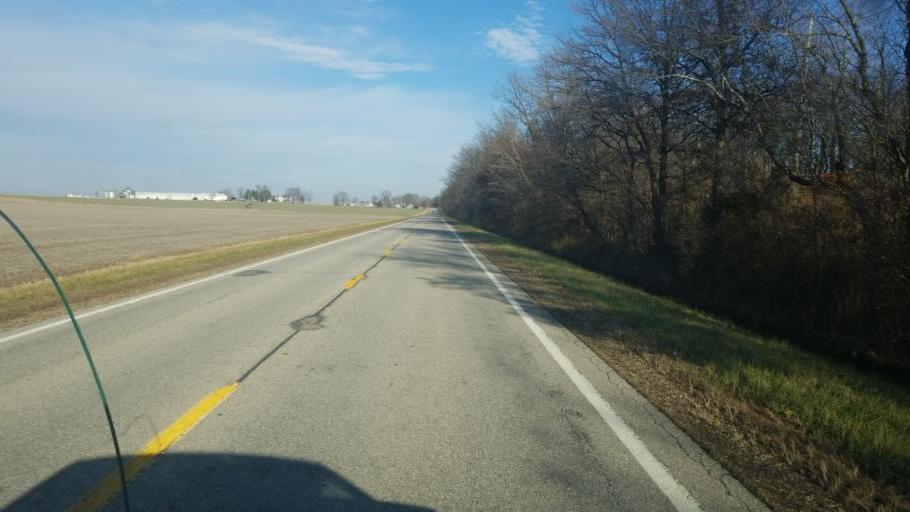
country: US
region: Illinois
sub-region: Wabash County
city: Mount Carmel
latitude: 38.3447
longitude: -87.8804
